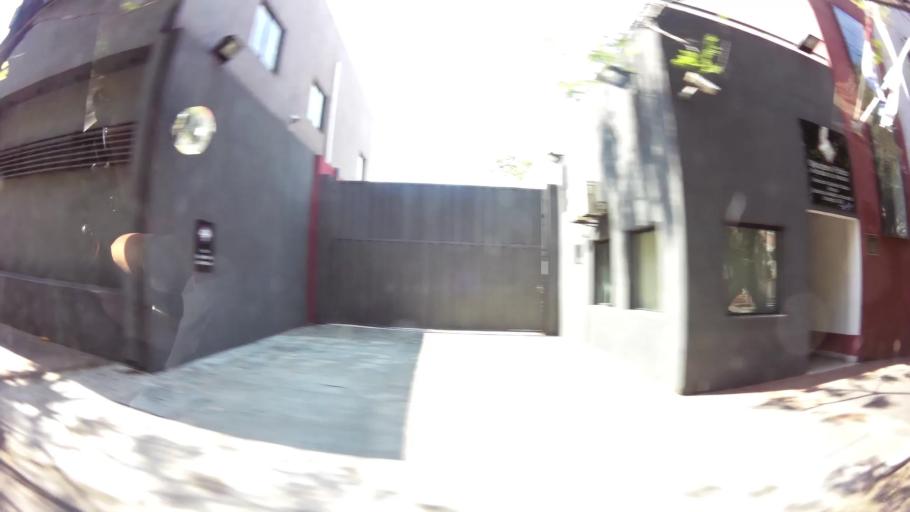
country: PY
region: Asuncion
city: Asuncion
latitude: -25.2897
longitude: -57.6412
